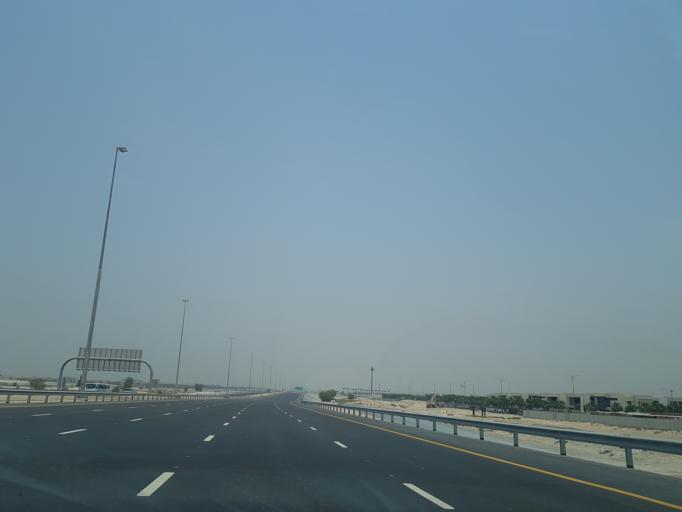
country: AE
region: Dubai
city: Dubai
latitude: 25.0260
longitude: 55.2437
